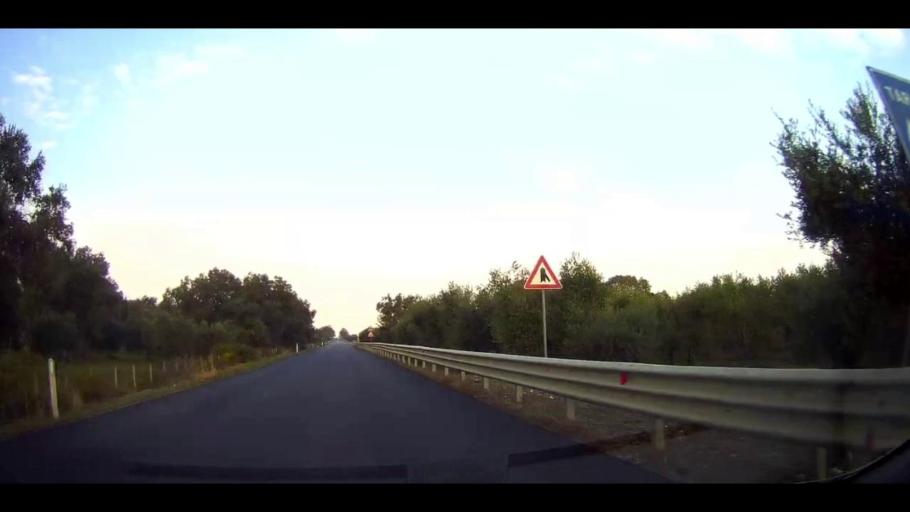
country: IT
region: Calabria
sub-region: Provincia di Crotone
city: Torretta
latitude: 39.4707
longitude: 17.0173
